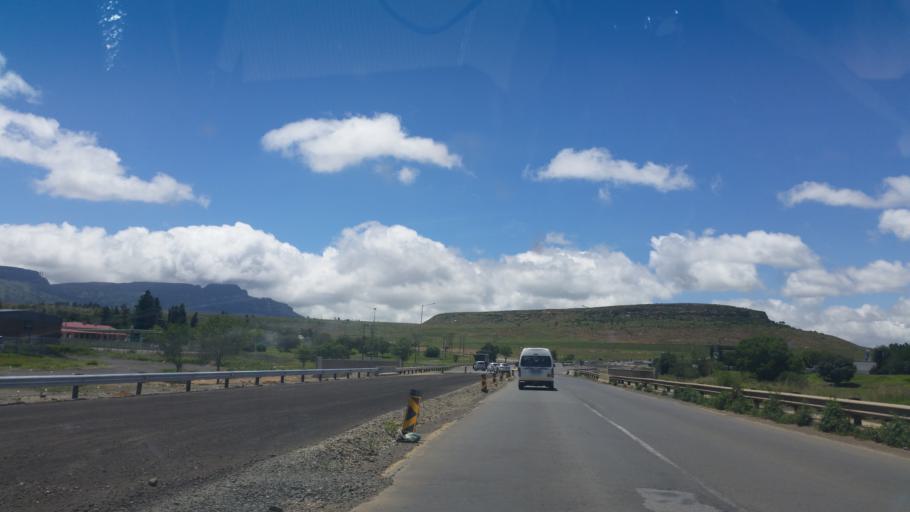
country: ZA
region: Orange Free State
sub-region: Thabo Mofutsanyana District Municipality
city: Harrismith
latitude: -28.2833
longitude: 29.1284
